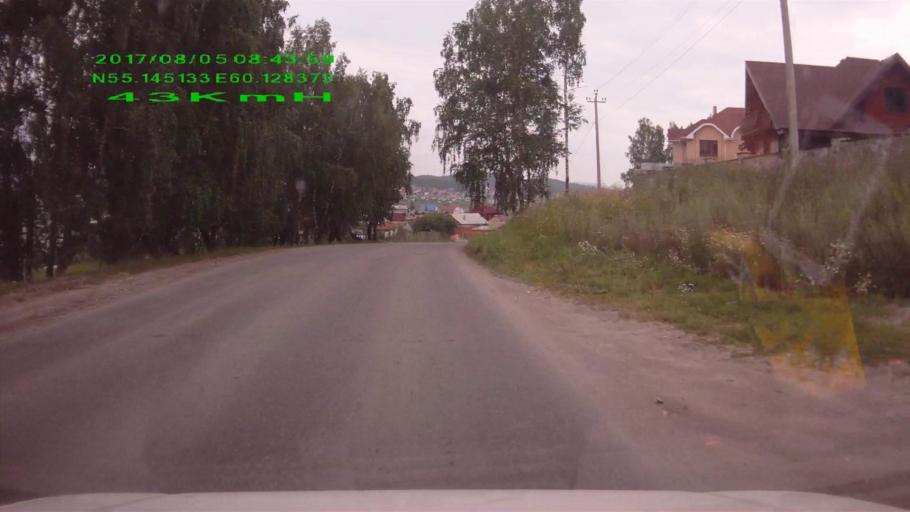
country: RU
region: Chelyabinsk
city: Turgoyak
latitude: 55.1451
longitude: 60.1283
